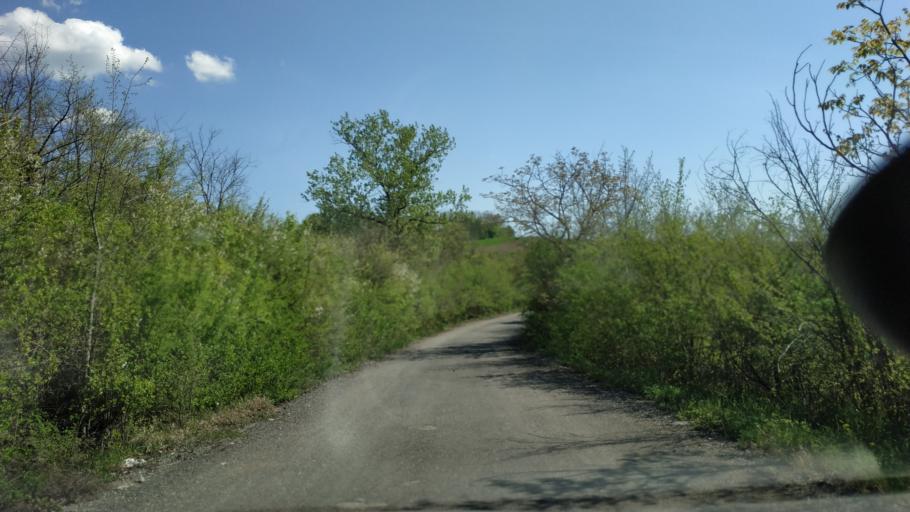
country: RS
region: Central Serbia
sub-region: Zajecarski Okrug
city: Soko Banja
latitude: 43.4923
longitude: 21.8731
